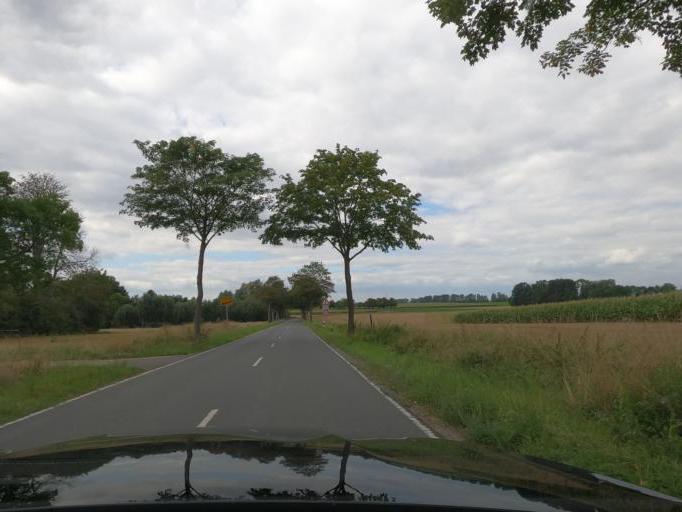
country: DE
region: Lower Saxony
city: Ilsede
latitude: 52.2180
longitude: 10.1595
